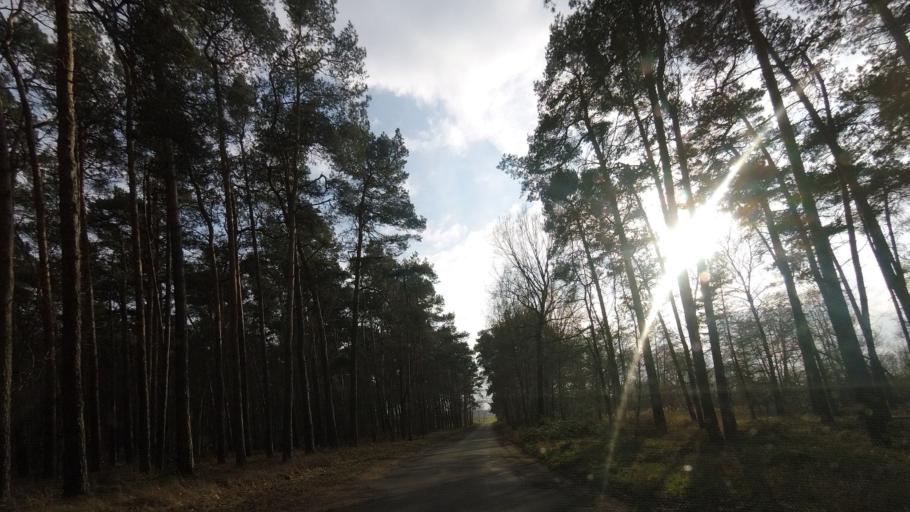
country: DE
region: Brandenburg
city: Belzig
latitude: 52.1794
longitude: 12.6350
